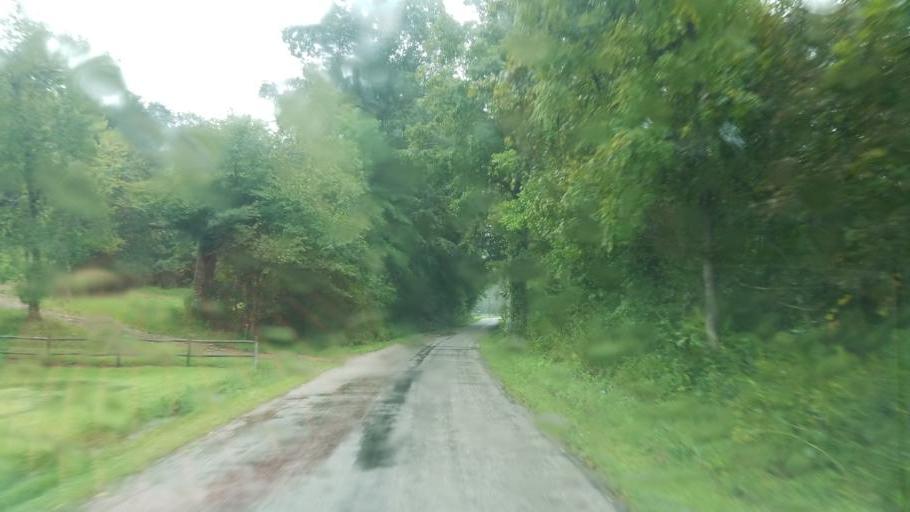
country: US
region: Ohio
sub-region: Adams County
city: Peebles
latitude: 38.8147
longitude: -83.2417
